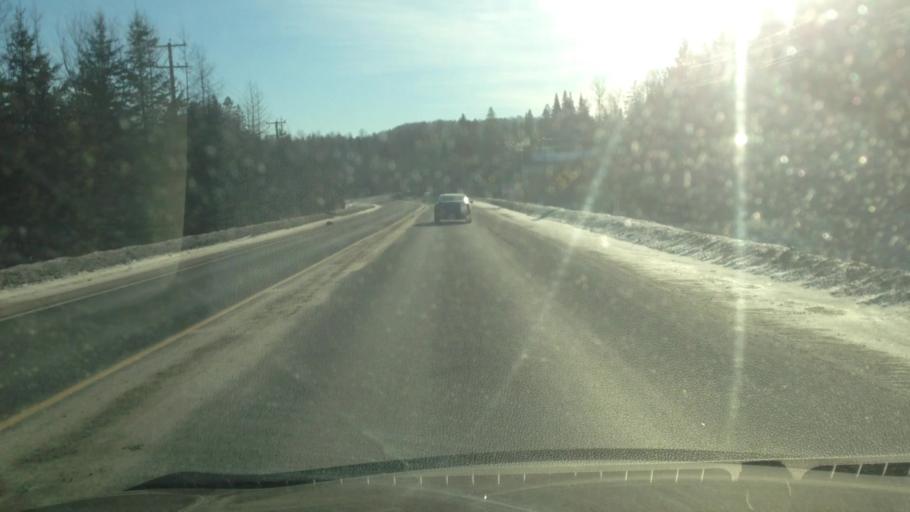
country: CA
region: Quebec
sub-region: Laurentides
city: Saint-Sauveur
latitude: 45.8882
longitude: -74.1892
